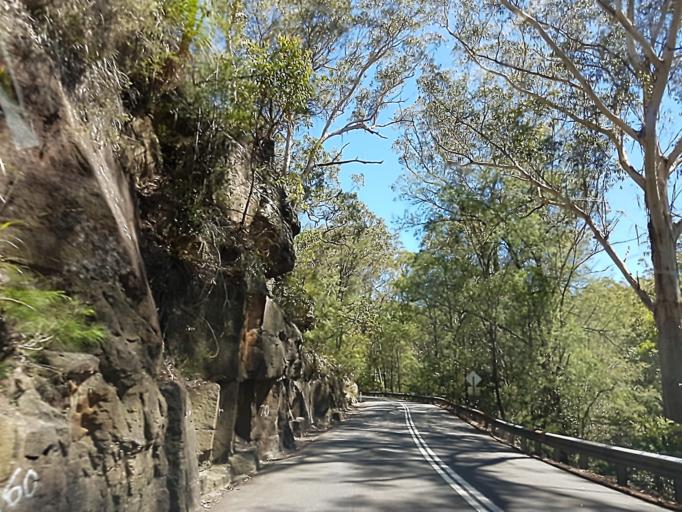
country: AU
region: New South Wales
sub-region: Hornsby Shire
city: Hornsby Heights
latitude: -33.6614
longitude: 151.0792
